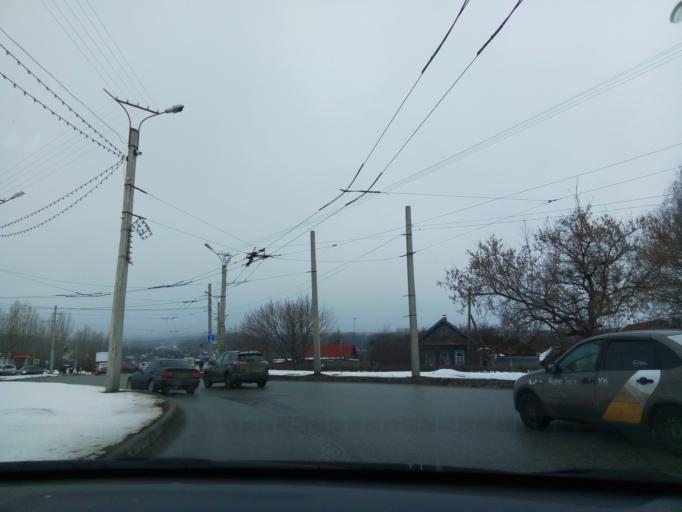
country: RU
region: Chuvashia
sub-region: Cheboksarskiy Rayon
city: Cheboksary
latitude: 56.1277
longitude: 47.2129
